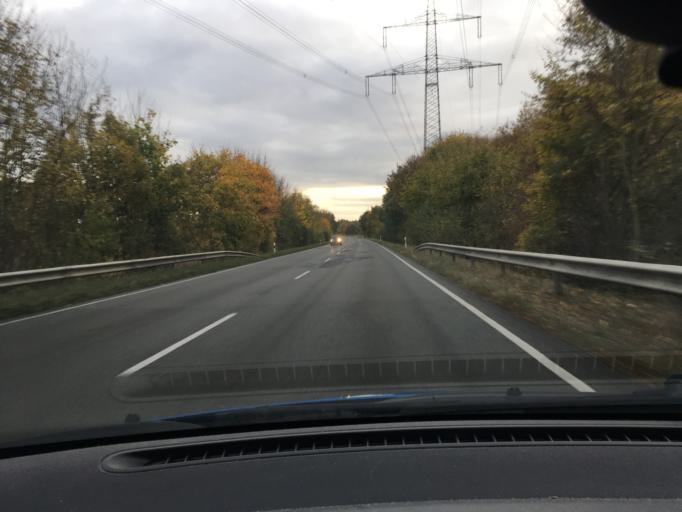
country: DE
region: Lower Saxony
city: Handorf
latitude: 53.3511
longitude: 10.3387
